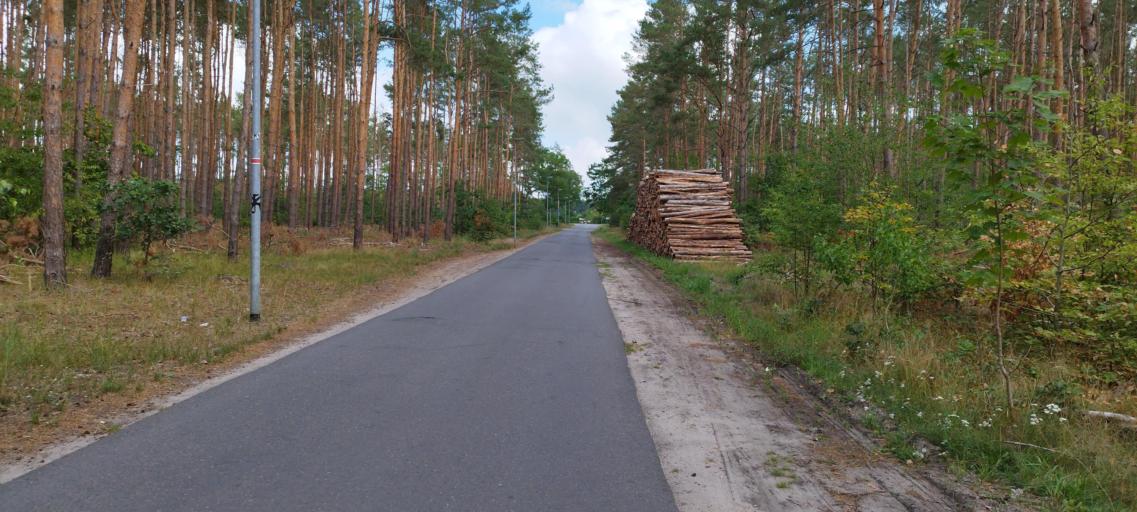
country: DE
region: Brandenburg
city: Rathenow
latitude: 52.5979
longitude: 12.3782
